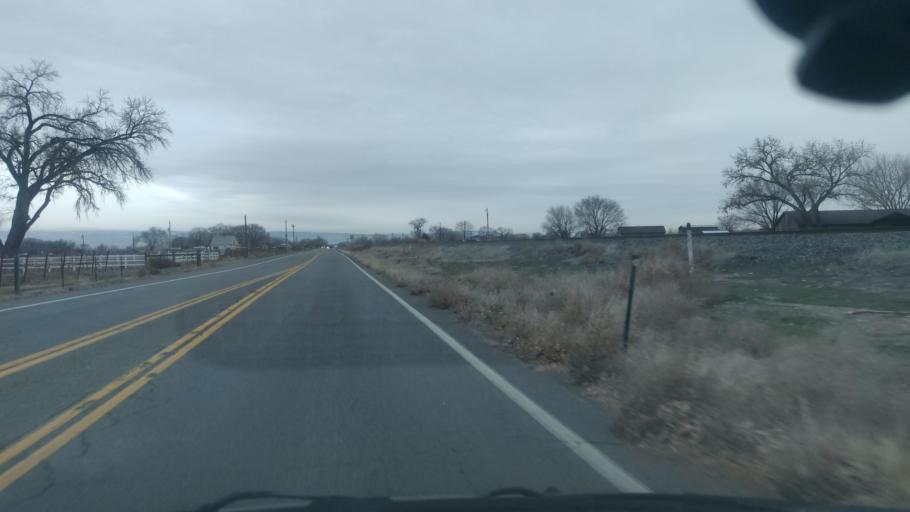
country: US
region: Colorado
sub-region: Mesa County
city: Clifton
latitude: 39.0972
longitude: -108.4098
